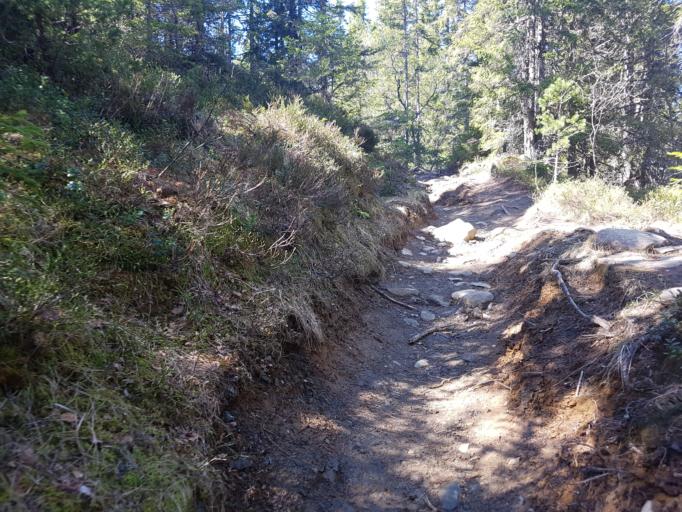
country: NO
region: Sor-Trondelag
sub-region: Trondheim
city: Trondheim
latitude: 63.4365
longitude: 10.3342
